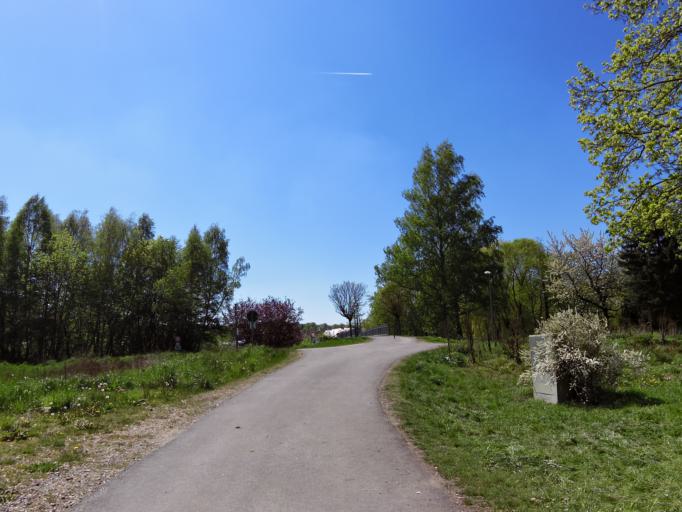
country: DE
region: Thuringia
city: Bad Salzungen
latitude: 50.8173
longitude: 10.2388
